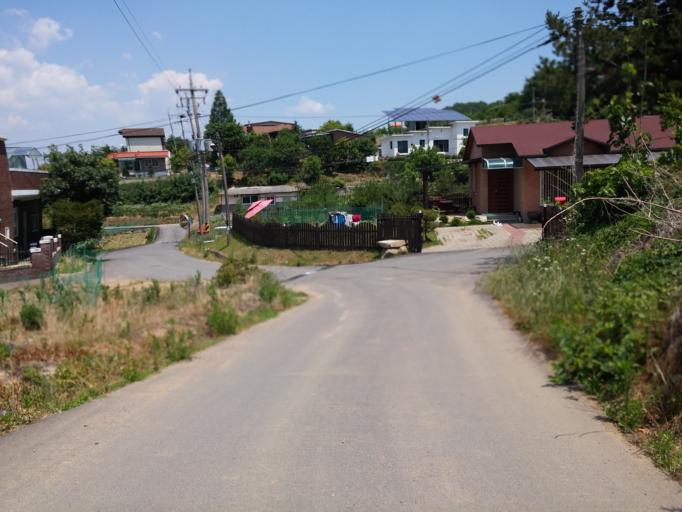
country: KR
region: Chungcheongbuk-do
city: Cheongju-si
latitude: 36.5532
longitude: 127.4366
